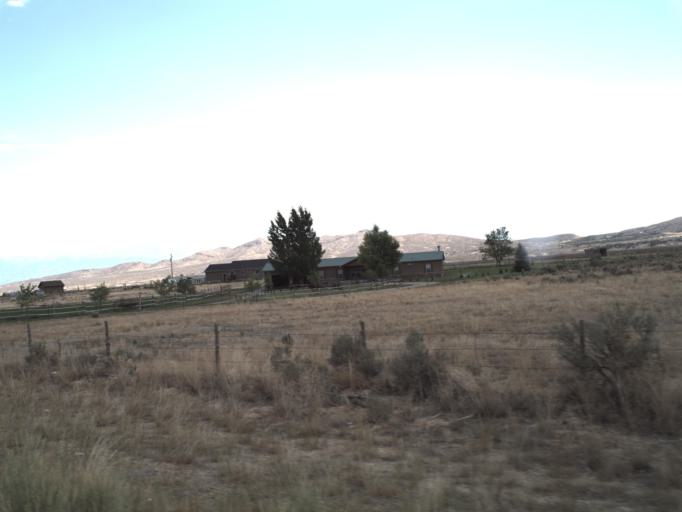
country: US
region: Utah
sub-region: Tooele County
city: Tooele
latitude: 40.0895
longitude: -112.4307
